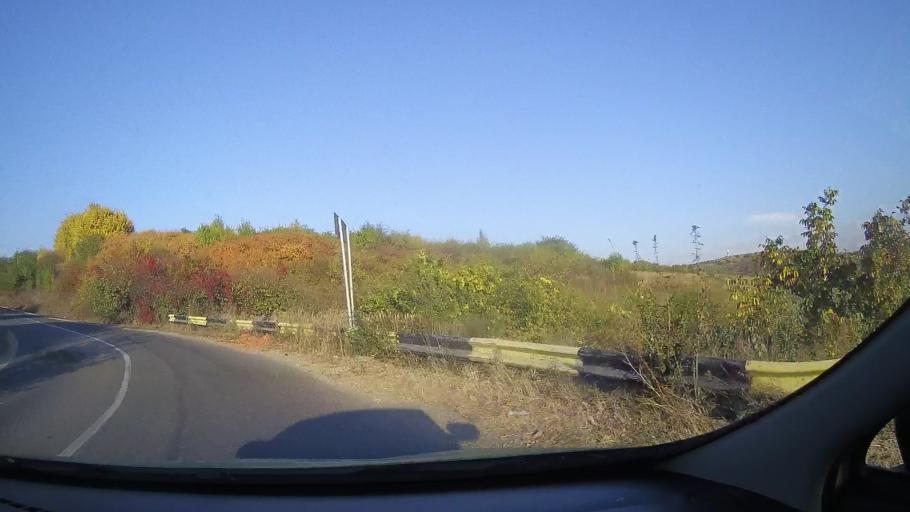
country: RO
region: Bihor
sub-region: Comuna Biharea
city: Oradea
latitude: 47.0968
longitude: 21.9244
